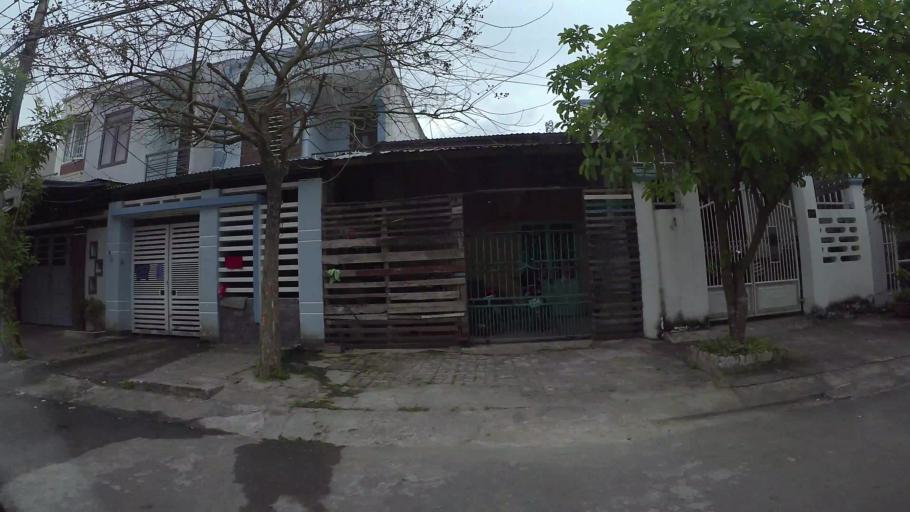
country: VN
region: Da Nang
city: Thanh Khe
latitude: 16.0444
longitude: 108.1740
